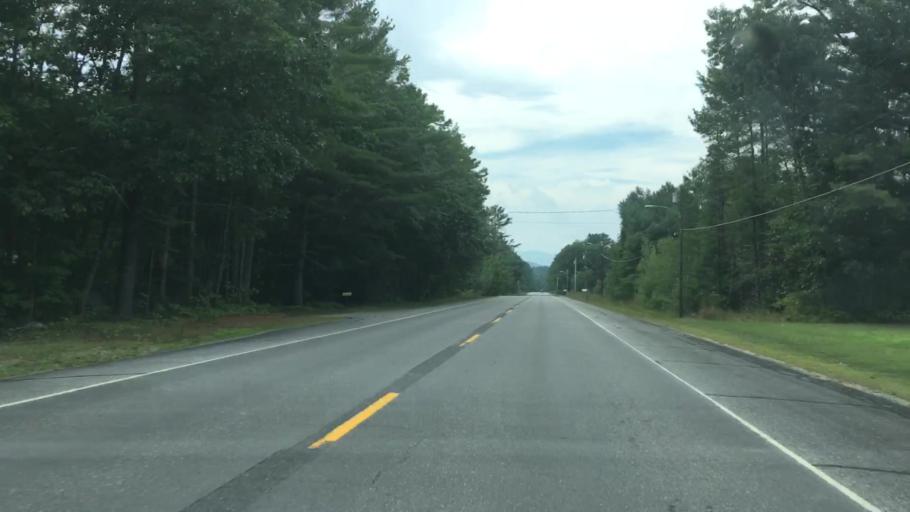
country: US
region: Maine
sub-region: Oxford County
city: Bethel
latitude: 44.4848
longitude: -70.7331
